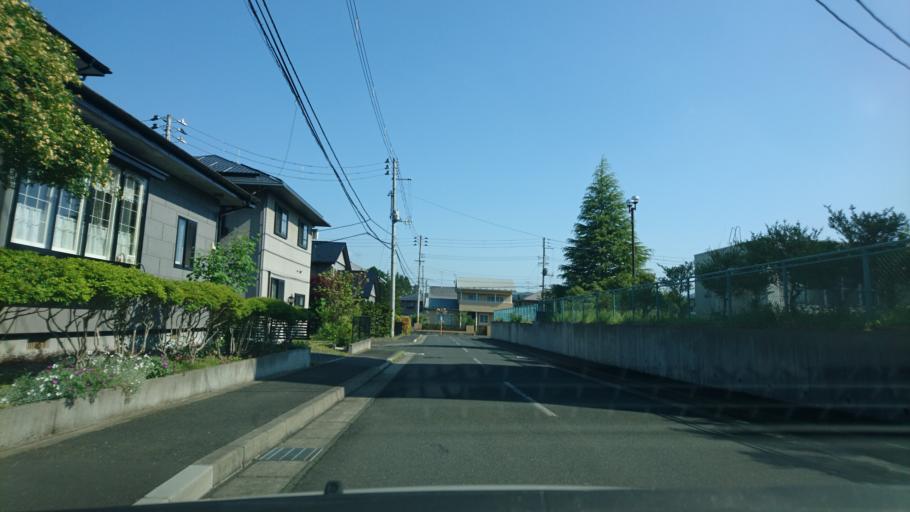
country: JP
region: Iwate
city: Ichinoseki
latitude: 38.9040
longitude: 141.1374
